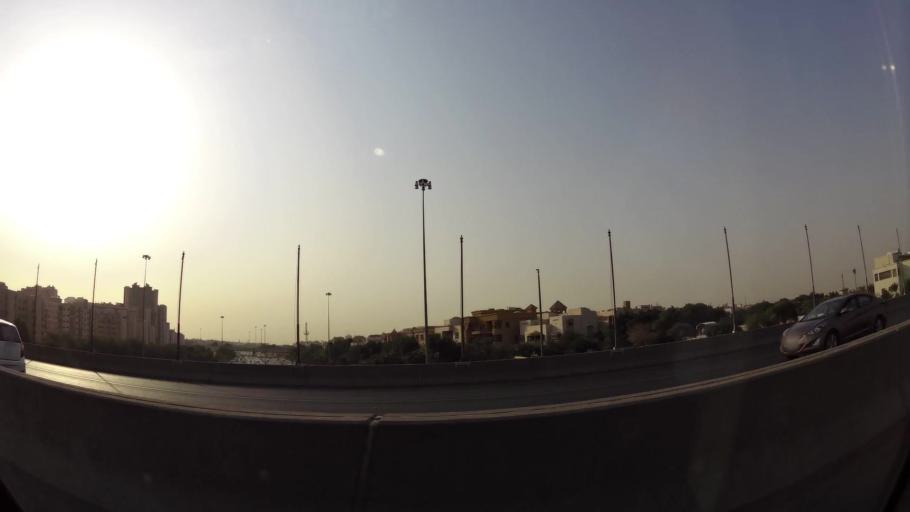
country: KW
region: Muhafazat Hawalli
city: Hawalli
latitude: 29.3229
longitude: 48.0119
